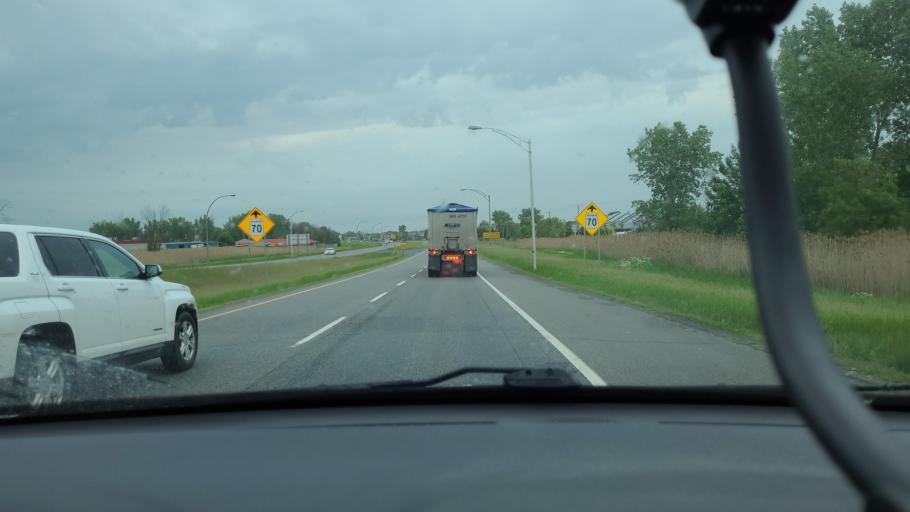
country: CA
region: Quebec
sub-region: Monteregie
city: Vaudreuil-Dorion
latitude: 45.3689
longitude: -74.0340
